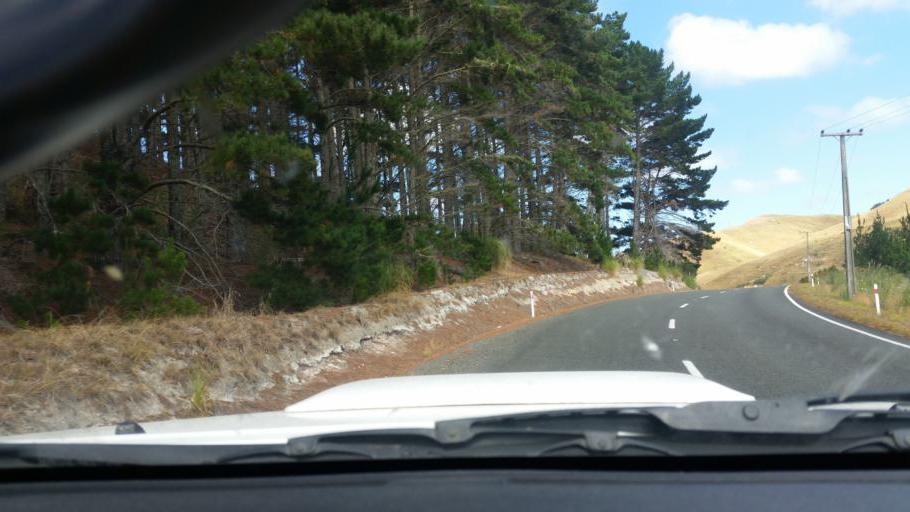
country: NZ
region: Northland
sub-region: Kaipara District
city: Dargaville
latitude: -35.8228
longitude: 173.7022
